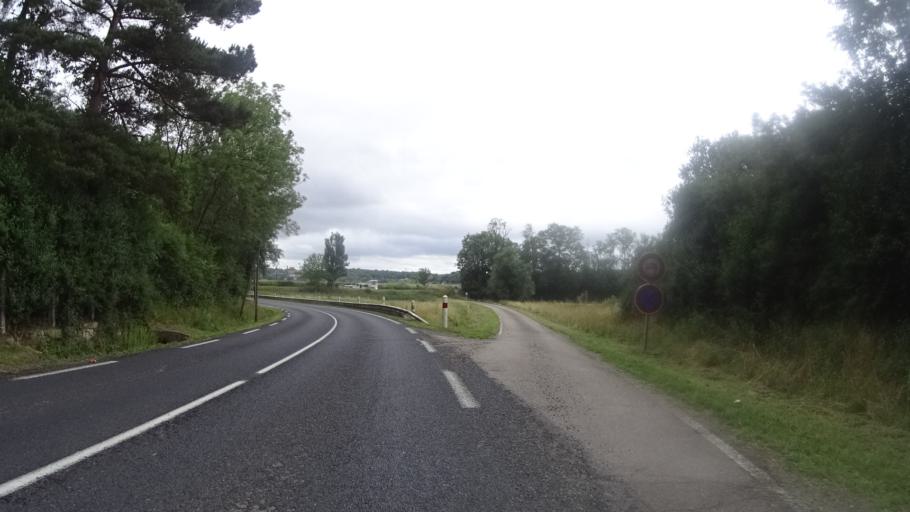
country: FR
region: Lorraine
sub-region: Departement de Meurthe-et-Moselle
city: Art-sur-Meurthe
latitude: 48.6474
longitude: 6.2788
